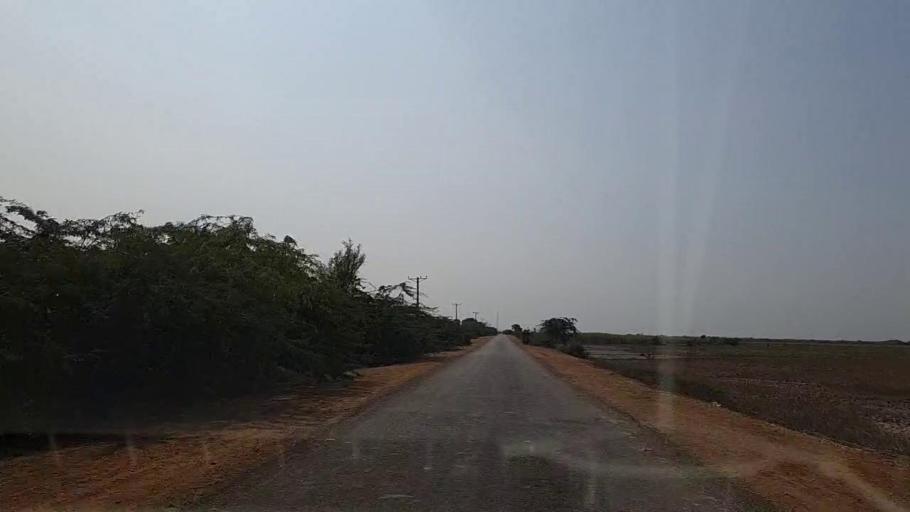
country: PK
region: Sindh
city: Chuhar Jamali
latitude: 24.2991
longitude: 67.9319
